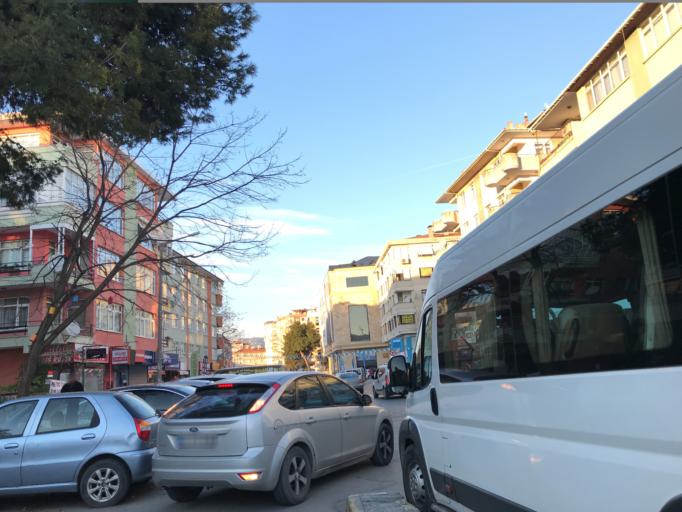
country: TR
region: Istanbul
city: Maltepe
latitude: 40.9266
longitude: 29.1330
